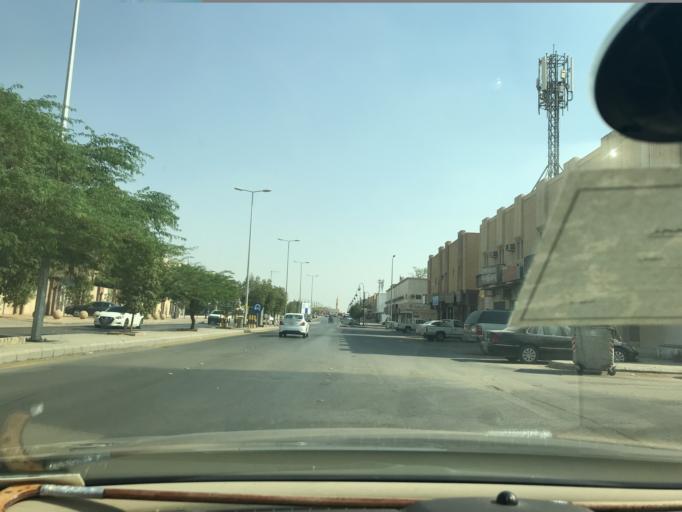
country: SA
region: Ar Riyad
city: Riyadh
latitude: 24.7444
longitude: 46.7645
